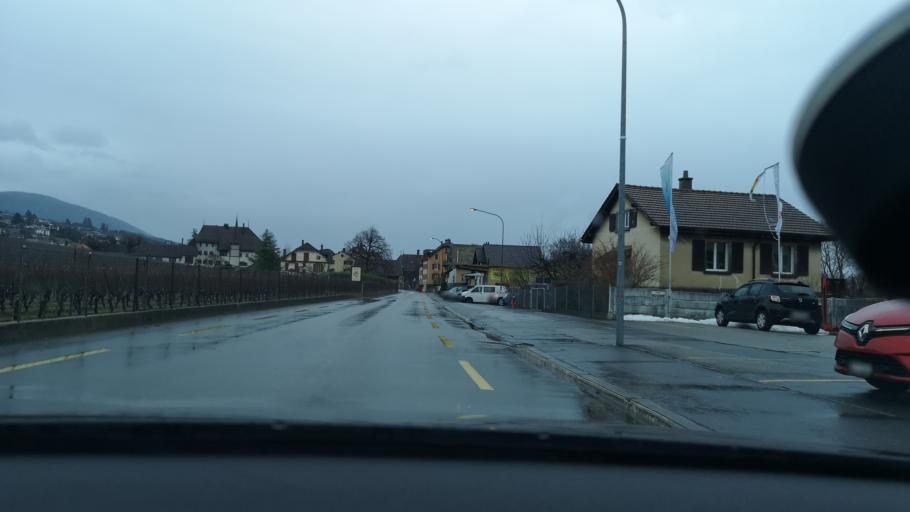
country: CH
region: Neuchatel
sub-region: Boudry District
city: Auvernier
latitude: 46.9732
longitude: 6.8733
